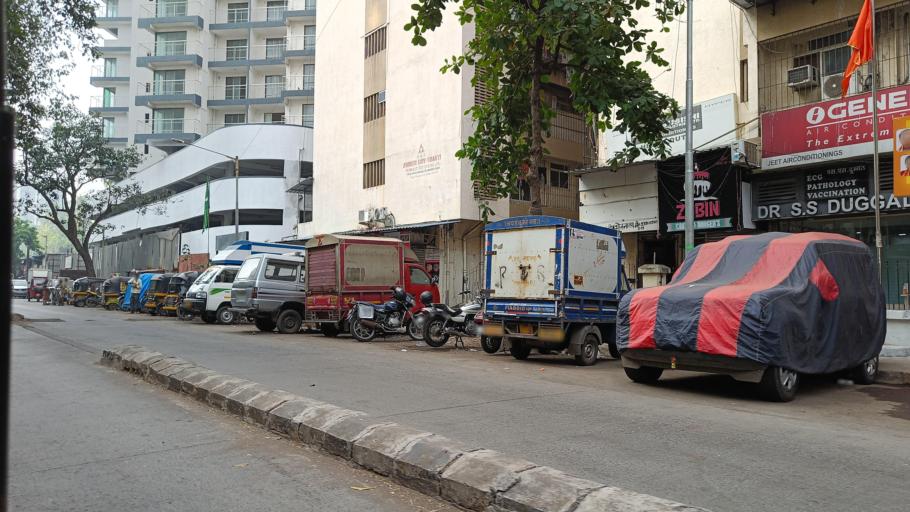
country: IN
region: Maharashtra
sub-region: Mumbai Suburban
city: Mumbai
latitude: 19.1268
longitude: 72.8290
